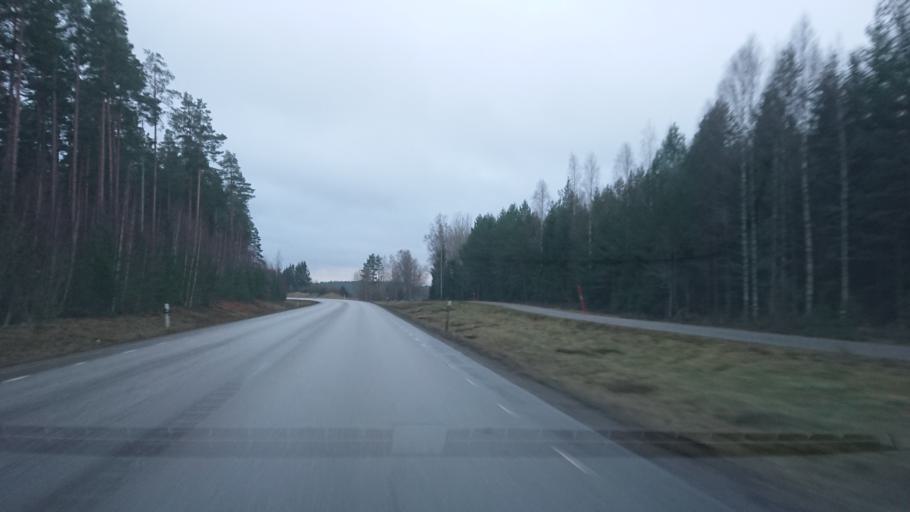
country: SE
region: Uppsala
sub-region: Osthammars Kommun
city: Bjorklinge
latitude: 60.0150
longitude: 17.5864
